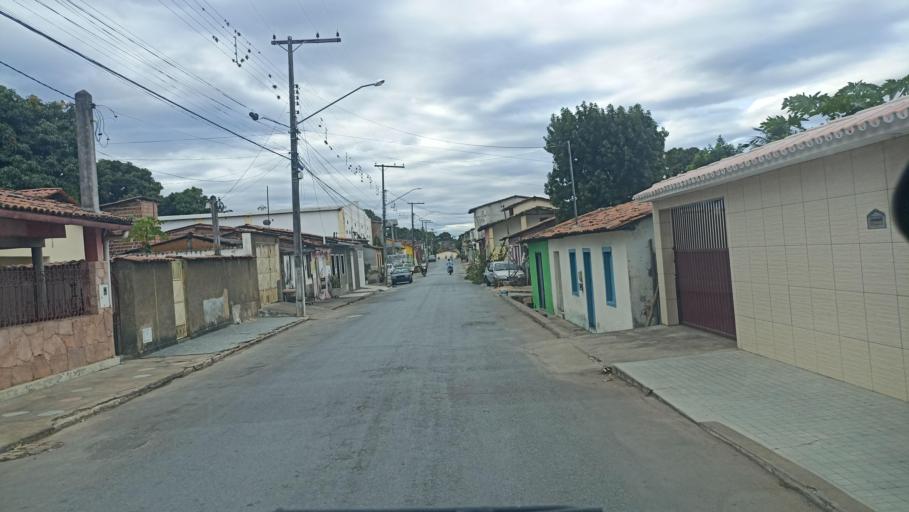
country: BR
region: Bahia
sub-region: Andarai
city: Vera Cruz
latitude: -12.8132
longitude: -41.3319
